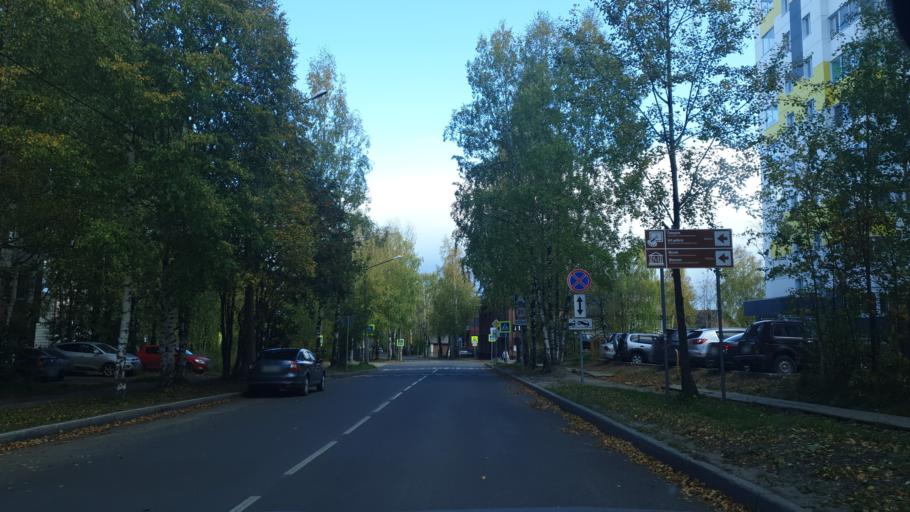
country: RU
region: Komi Republic
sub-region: Syktyvdinskiy Rayon
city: Syktyvkar
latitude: 61.6600
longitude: 50.8367
